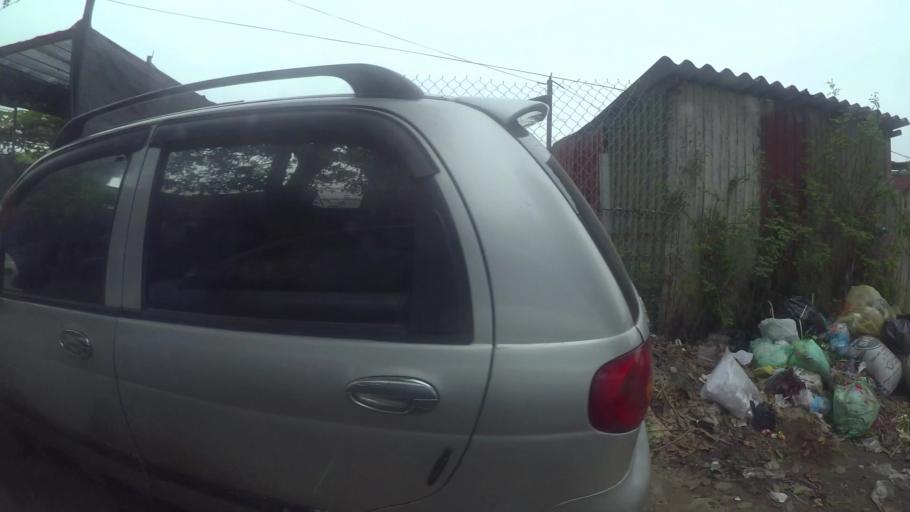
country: VN
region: Ha Noi
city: Tay Ho
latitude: 21.0590
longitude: 105.8393
